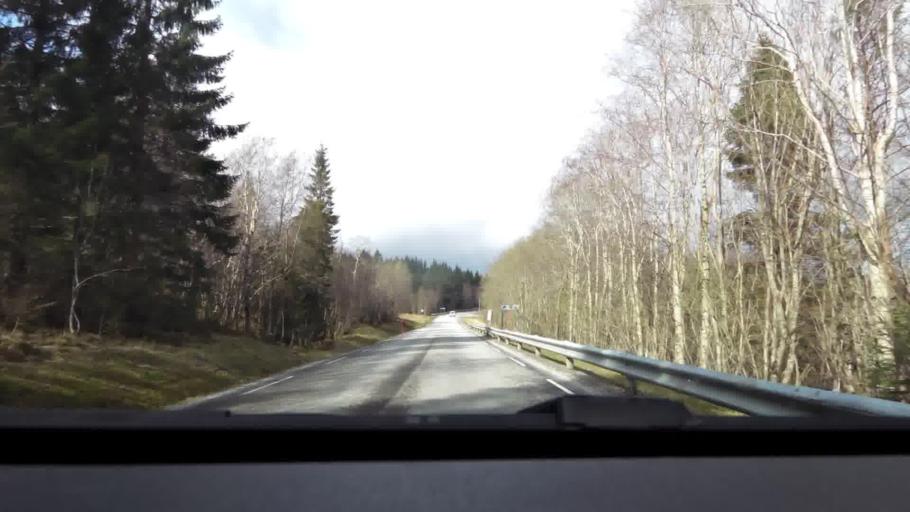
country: NO
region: More og Romsdal
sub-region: Averoy
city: Bruhagen
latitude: 63.1030
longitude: 7.6273
